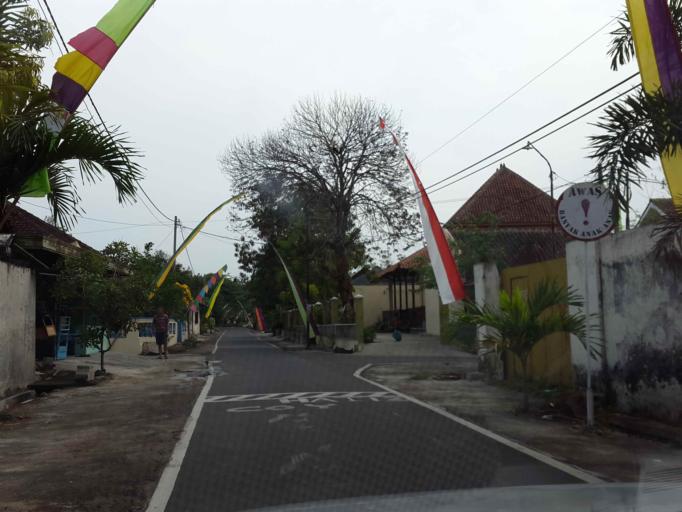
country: ID
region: Central Java
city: Jaten
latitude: -7.5996
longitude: 110.9597
